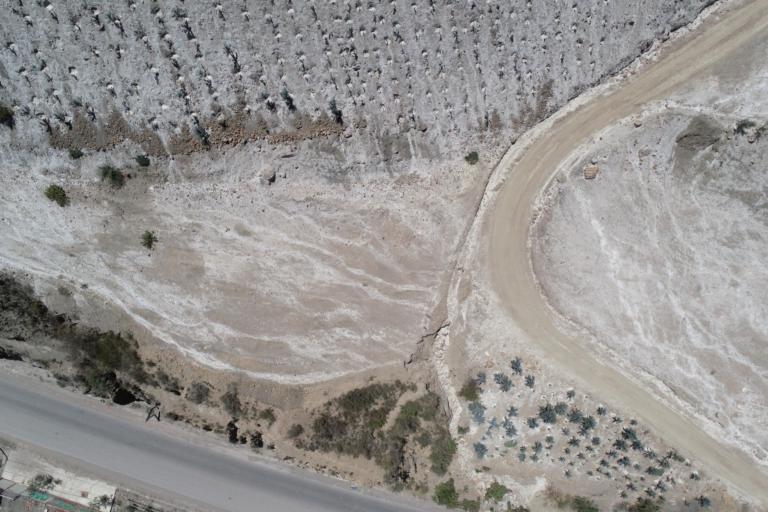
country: BO
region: La Paz
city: La Paz
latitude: -16.6163
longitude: -68.0582
